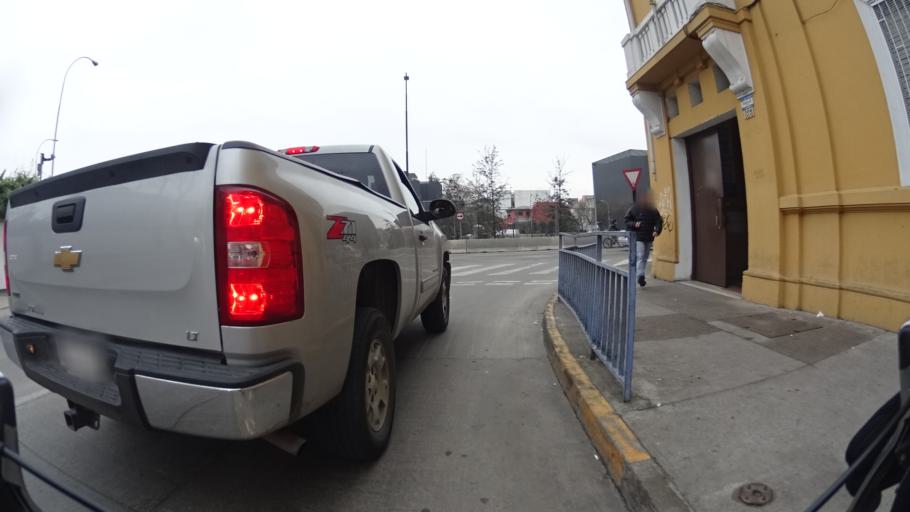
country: CL
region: Santiago Metropolitan
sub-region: Provincia de Santiago
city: Santiago
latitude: -33.4507
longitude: -70.6586
